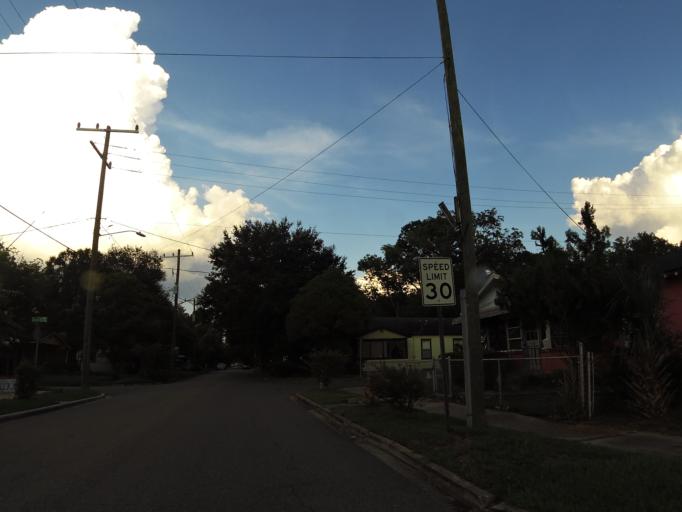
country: US
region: Florida
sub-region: Duval County
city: Jacksonville
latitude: 30.3406
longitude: -81.6863
